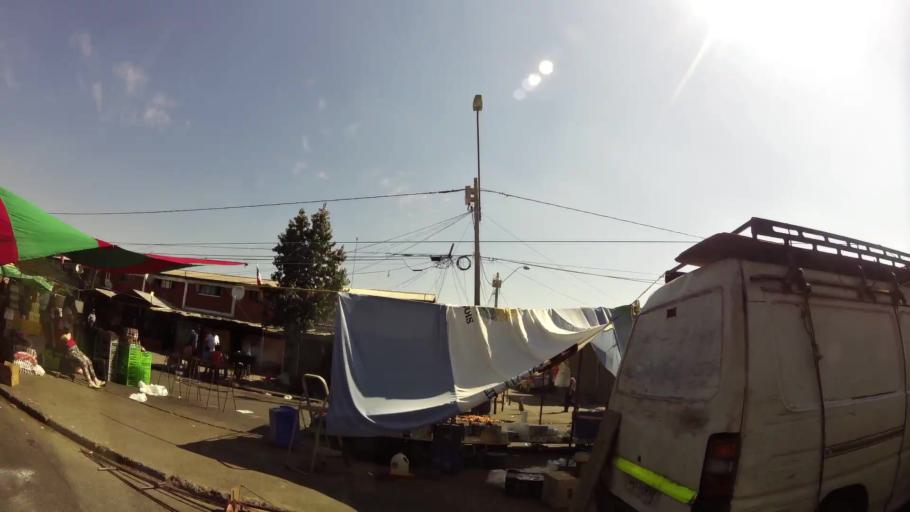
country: CL
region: Santiago Metropolitan
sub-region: Provincia de Santiago
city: La Pintana
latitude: -33.5599
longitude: -70.6232
